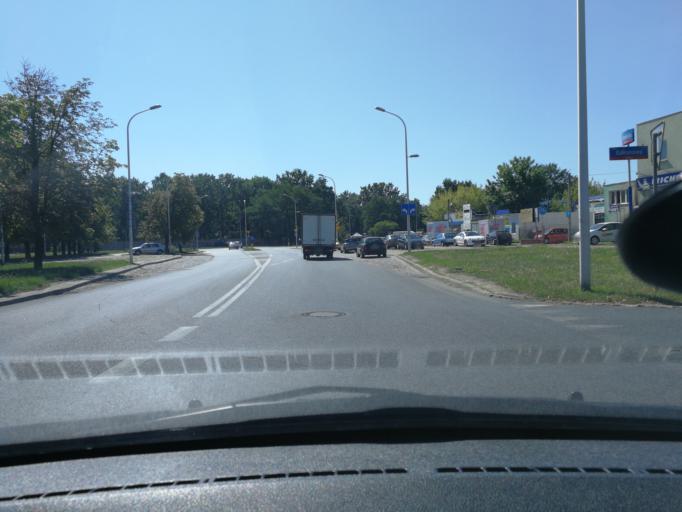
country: PL
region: Masovian Voivodeship
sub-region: Warszawa
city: Targowek
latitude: 52.2859
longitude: 21.0404
